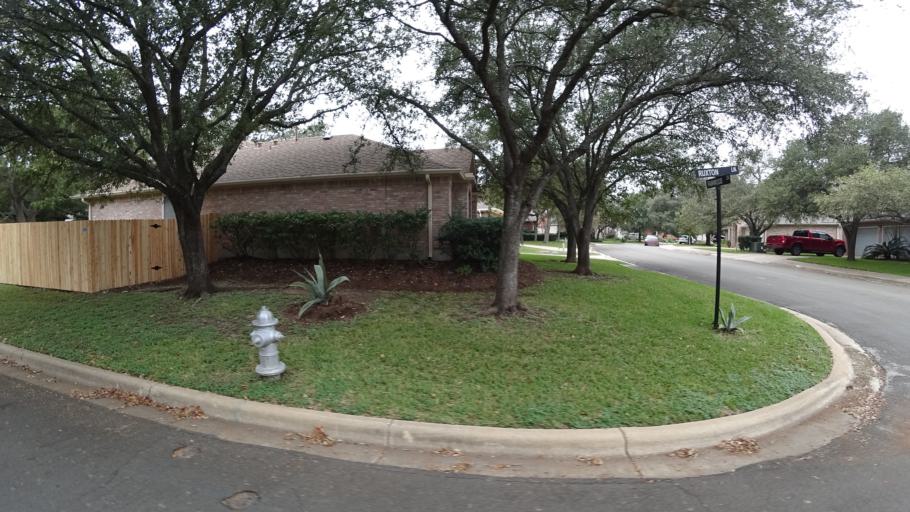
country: US
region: Texas
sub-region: Travis County
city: Shady Hollow
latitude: 30.2100
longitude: -97.8844
